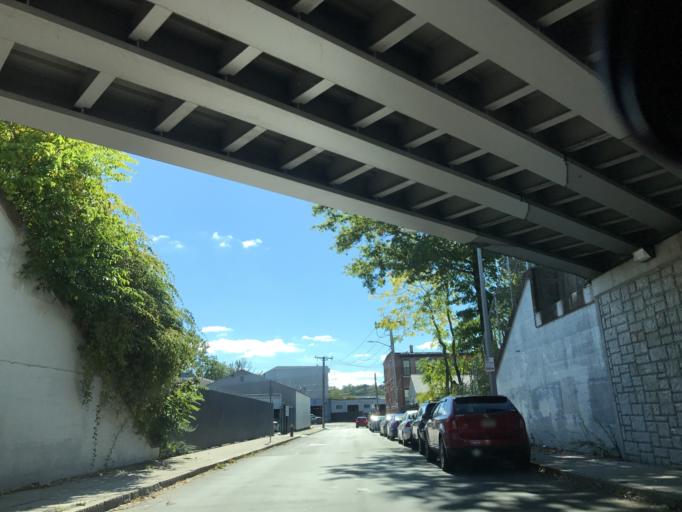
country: US
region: Massachusetts
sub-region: Suffolk County
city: South Boston
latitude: 42.3014
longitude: -71.0561
